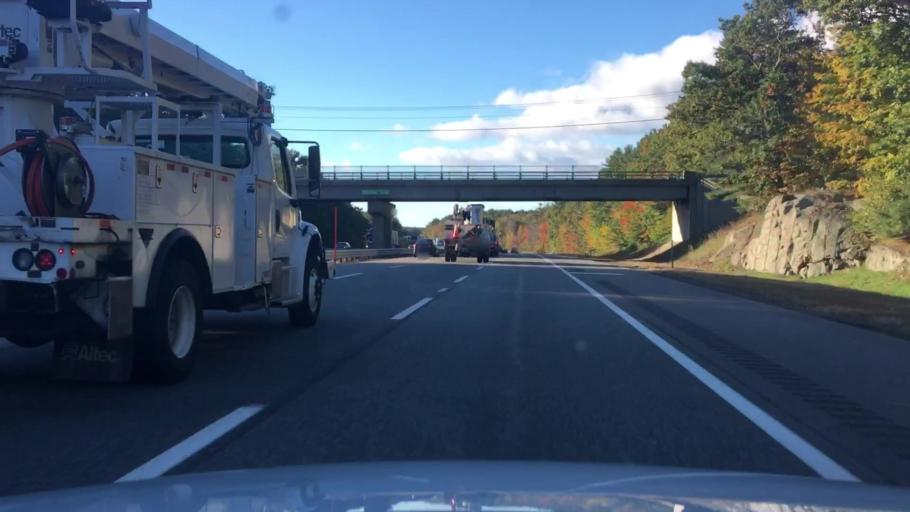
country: US
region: Maine
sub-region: York County
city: Cape Neddick
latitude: 43.2056
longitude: -70.6432
